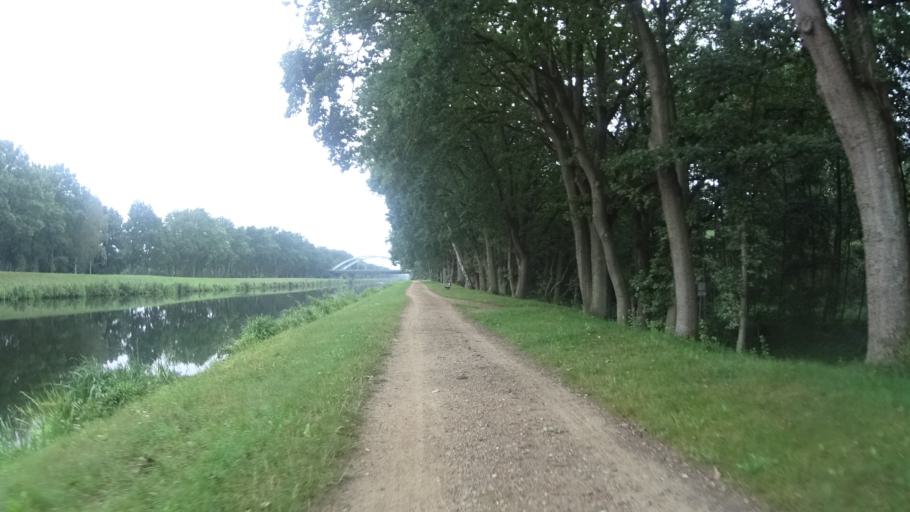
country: DE
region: Schleswig-Holstein
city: Buchen
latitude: 53.4746
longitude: 10.6310
